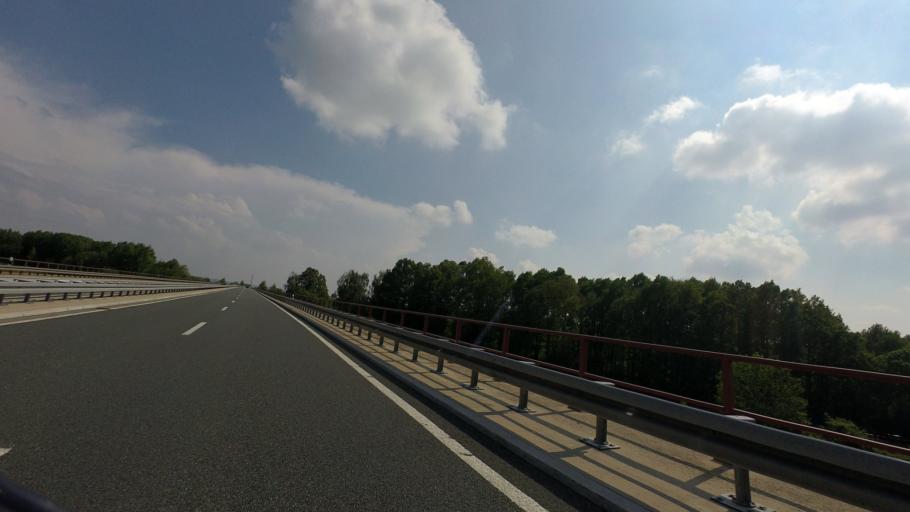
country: DE
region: Saxony
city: Lobau
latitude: 51.1237
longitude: 14.6472
